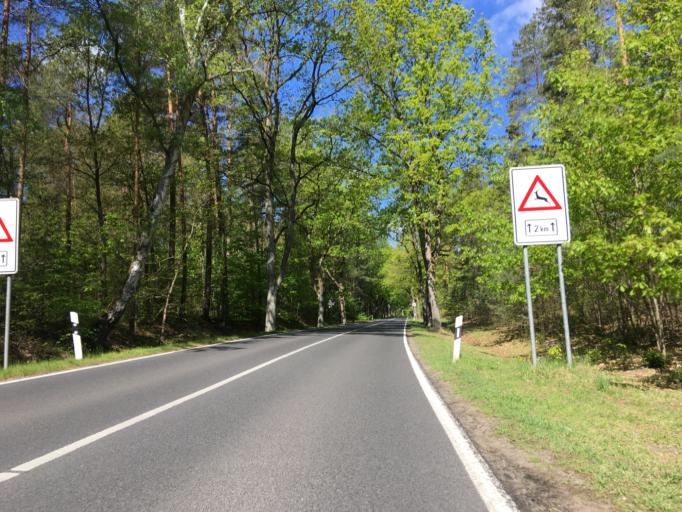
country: DE
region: Brandenburg
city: Birkenwerder
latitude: 52.7174
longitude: 13.3428
